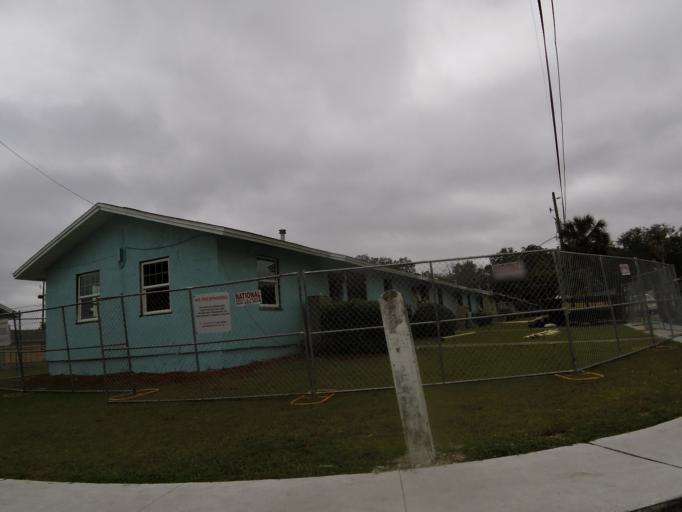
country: US
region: Florida
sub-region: Duval County
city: Jacksonville
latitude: 30.3681
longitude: -81.6844
